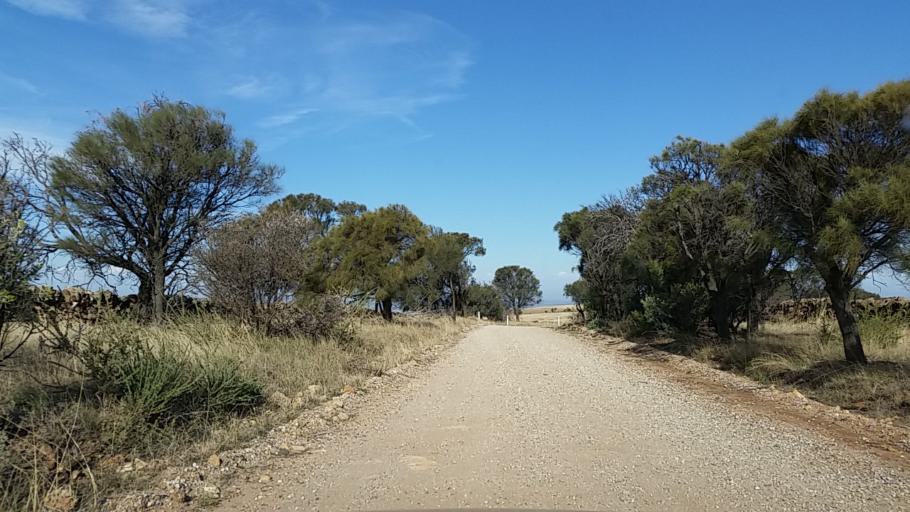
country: AU
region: South Australia
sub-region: Barossa
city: Angaston
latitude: -34.6144
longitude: 139.1985
